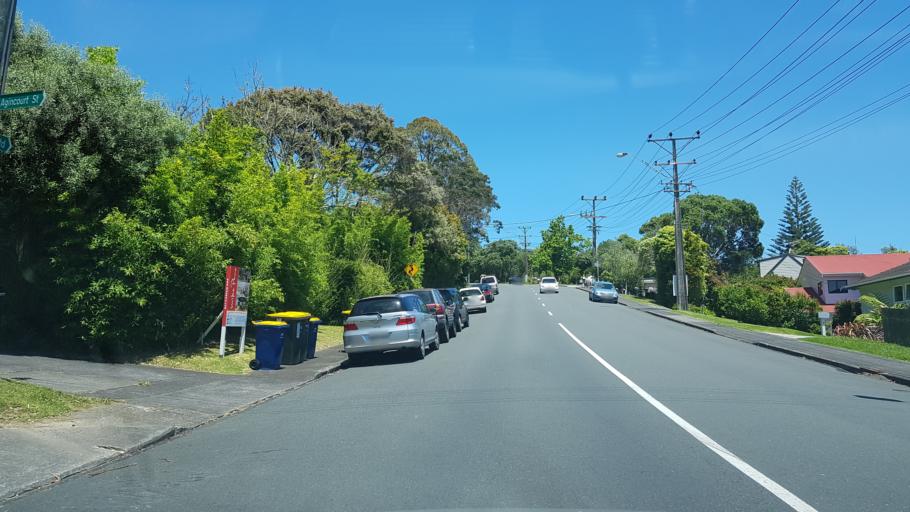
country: NZ
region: Auckland
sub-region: Auckland
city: North Shore
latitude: -36.7893
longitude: 174.7285
